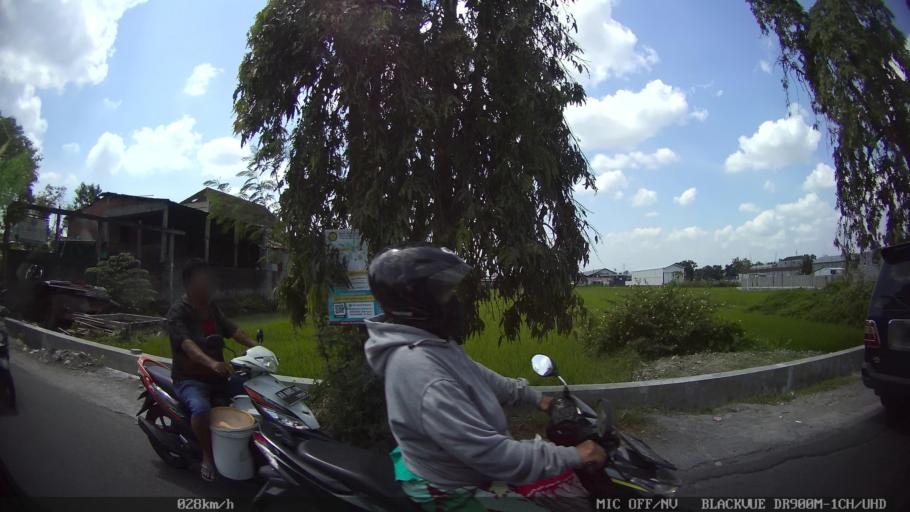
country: ID
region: Daerah Istimewa Yogyakarta
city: Kasihan
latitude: -7.8249
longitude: 110.3453
